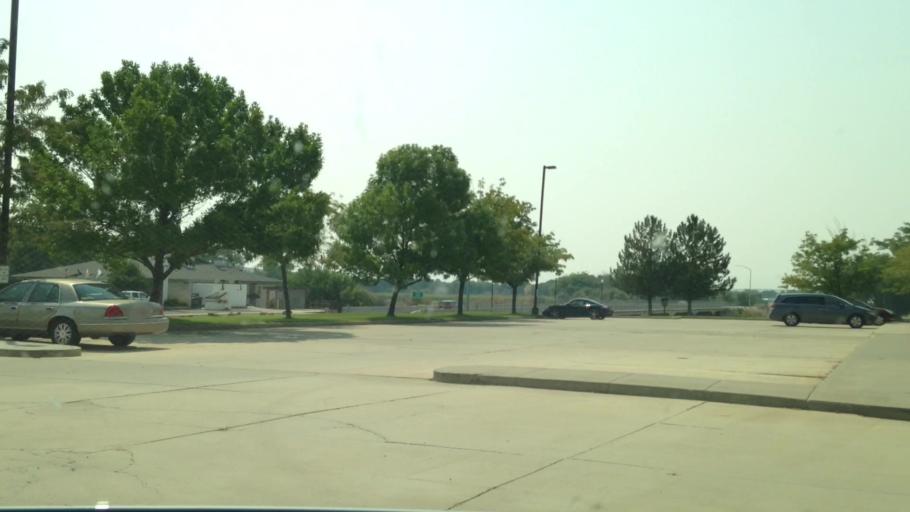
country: US
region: Utah
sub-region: Carbon County
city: East Carbon City
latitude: 38.9936
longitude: -110.1408
